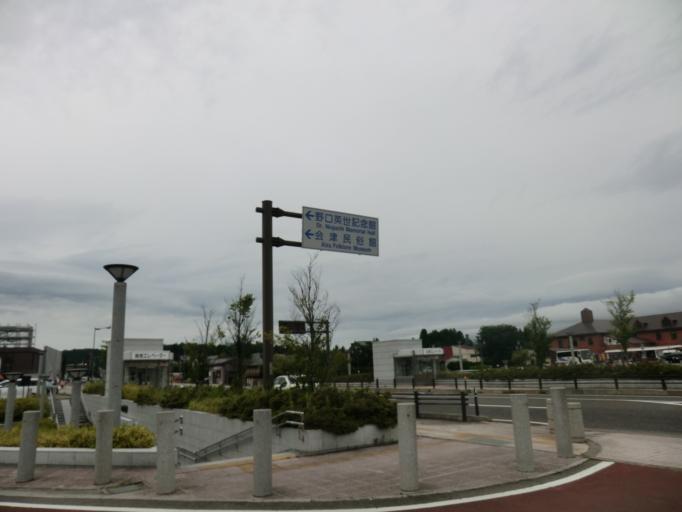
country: JP
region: Fukushima
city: Inawashiro
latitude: 37.5363
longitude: 140.0755
